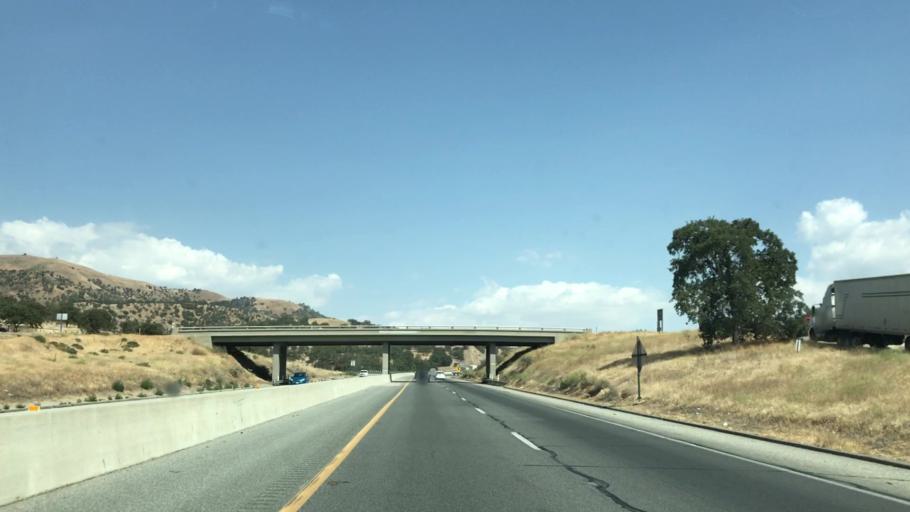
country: US
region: California
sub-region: Kern County
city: Golden Hills
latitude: 35.2005
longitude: -118.5232
